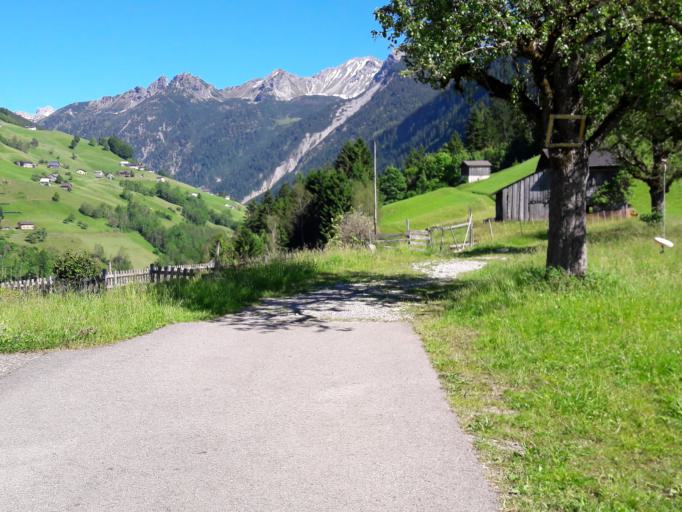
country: AT
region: Vorarlberg
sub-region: Politischer Bezirk Bludenz
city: Raggal
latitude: 47.2088
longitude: 9.8474
